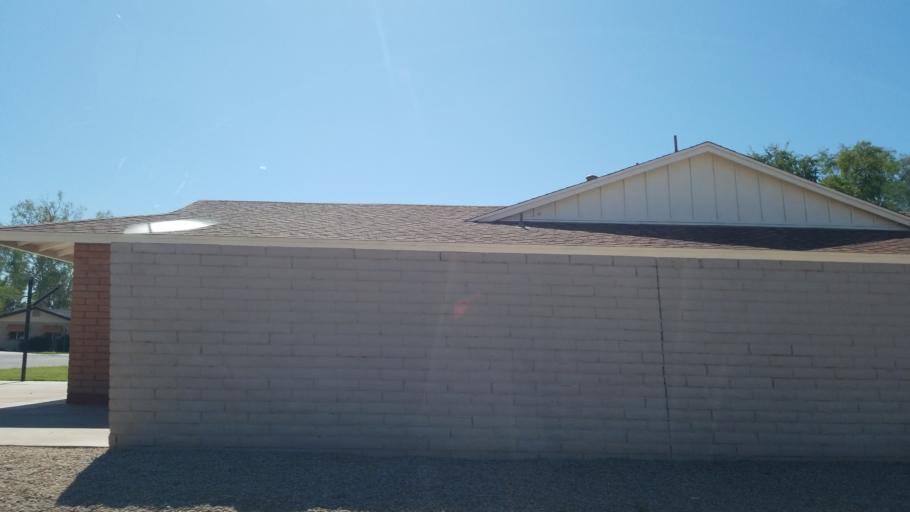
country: US
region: Arizona
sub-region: Maricopa County
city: Glendale
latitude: 33.5022
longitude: -112.1904
